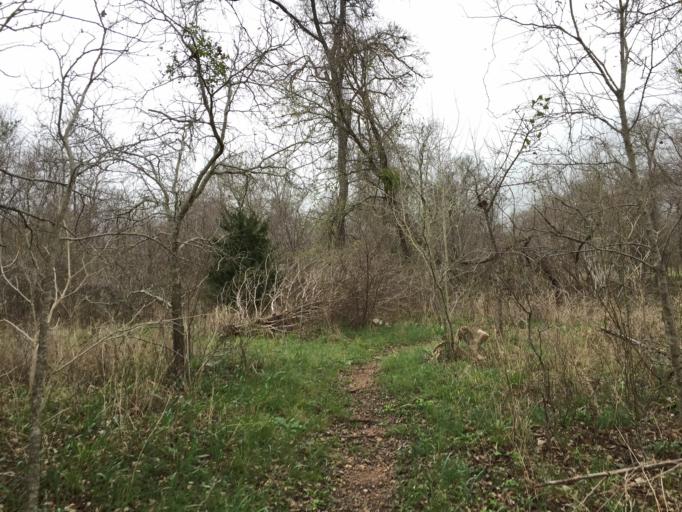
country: US
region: Texas
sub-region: Bastrop County
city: Bastrop
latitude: 30.0836
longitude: -97.3208
